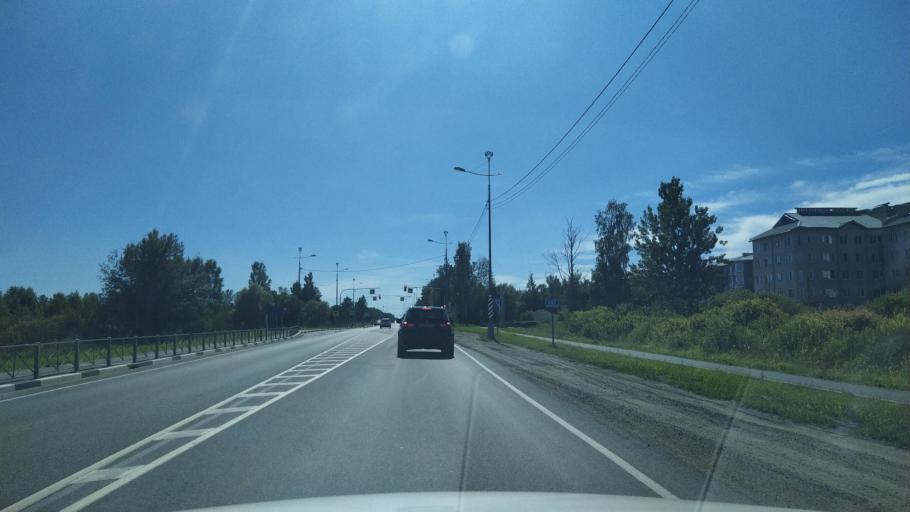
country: RU
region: Pskov
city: Pskov
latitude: 57.7913
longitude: 28.4135
